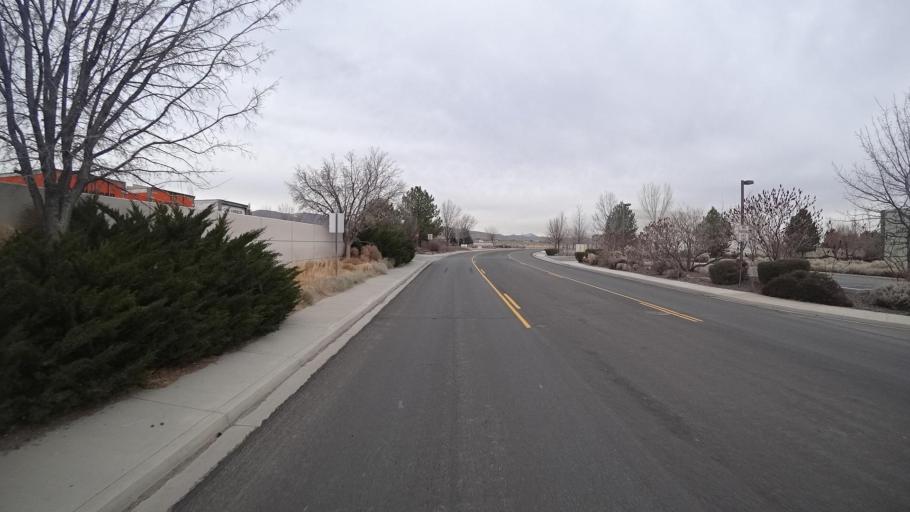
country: US
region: Nevada
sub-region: Washoe County
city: Spanish Springs
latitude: 39.6728
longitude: -119.7048
